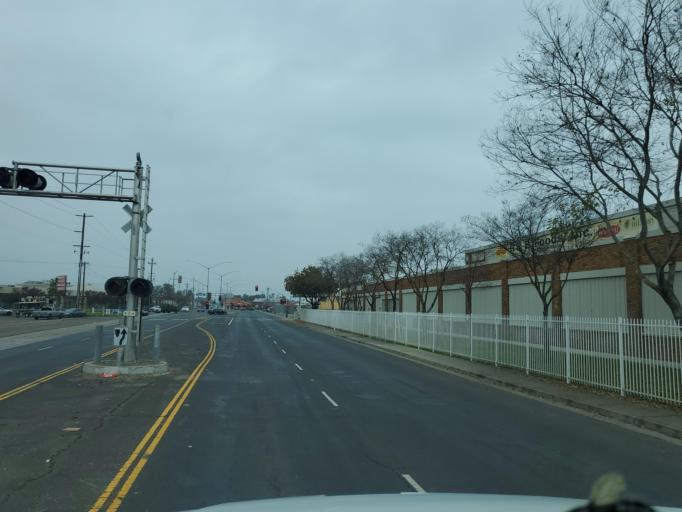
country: US
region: California
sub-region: San Joaquin County
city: August
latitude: 37.9708
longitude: -121.2696
